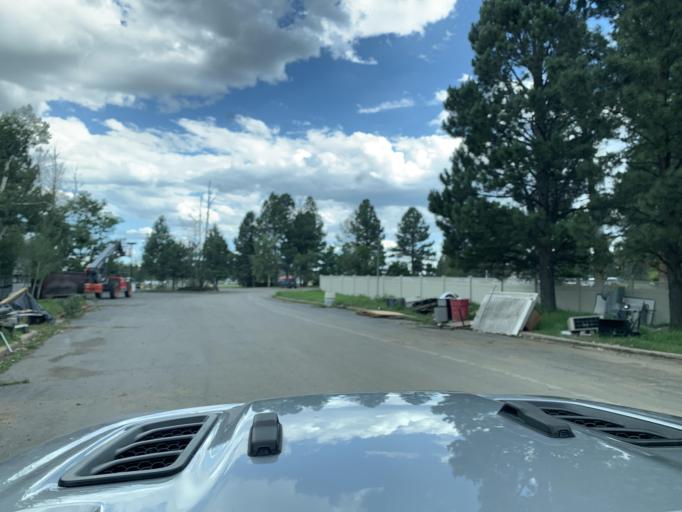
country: US
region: Colorado
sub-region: Archuleta County
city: Pagosa Springs
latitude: 37.2606
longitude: -107.0694
